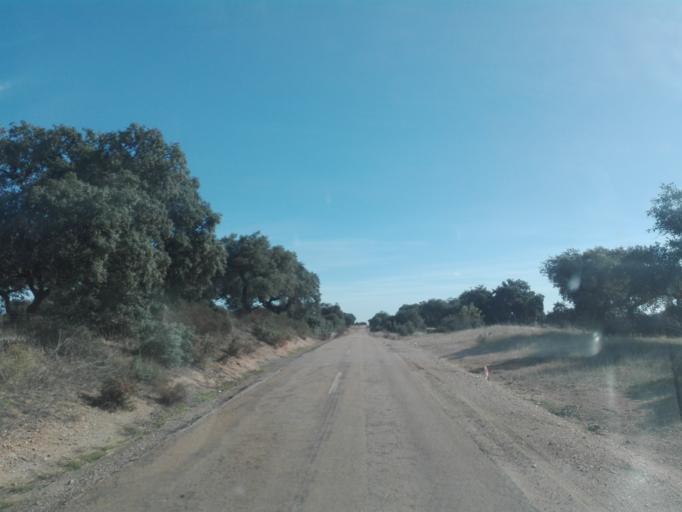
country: ES
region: Extremadura
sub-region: Provincia de Badajoz
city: Maguilla
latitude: 38.3403
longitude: -5.9154
